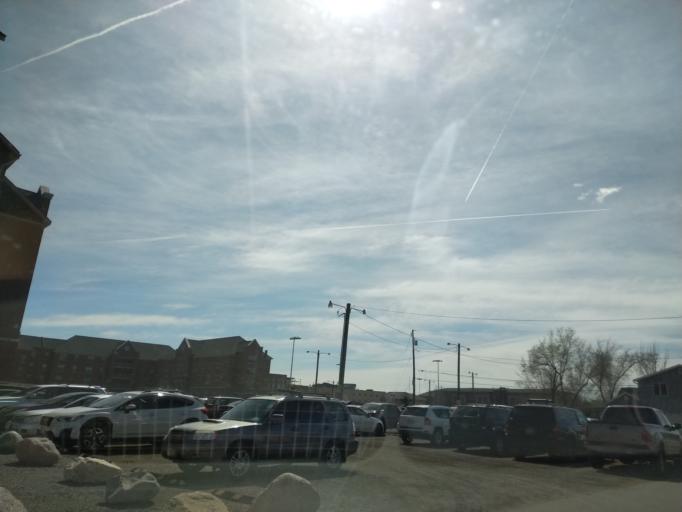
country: US
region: Colorado
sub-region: Mesa County
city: Grand Junction
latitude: 39.0819
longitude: -108.5582
